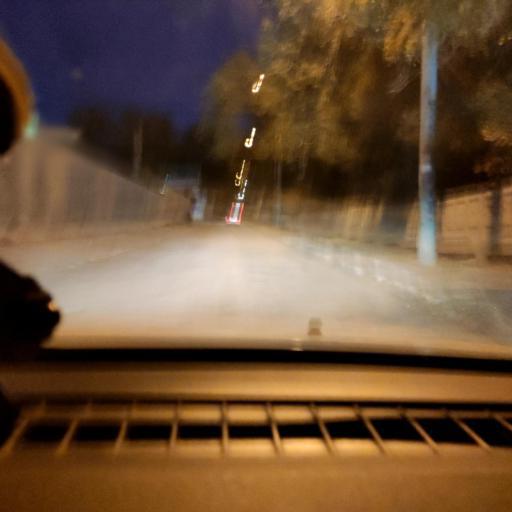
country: RU
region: Samara
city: Samara
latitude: 53.1908
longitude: 50.1548
